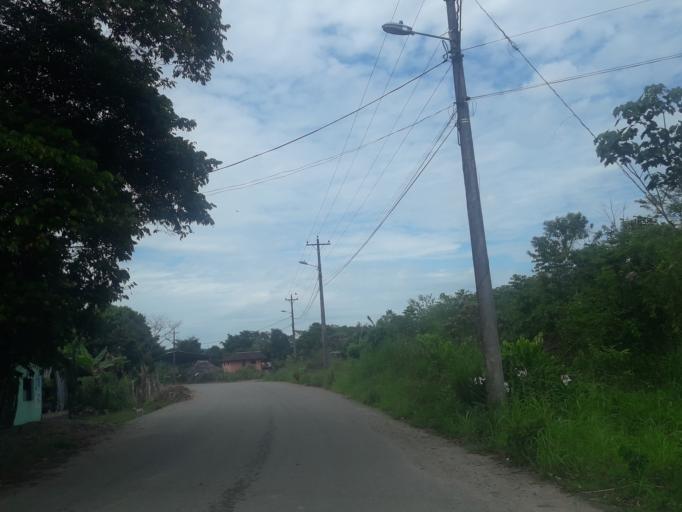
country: EC
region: Napo
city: Tena
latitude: -1.0492
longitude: -77.7967
